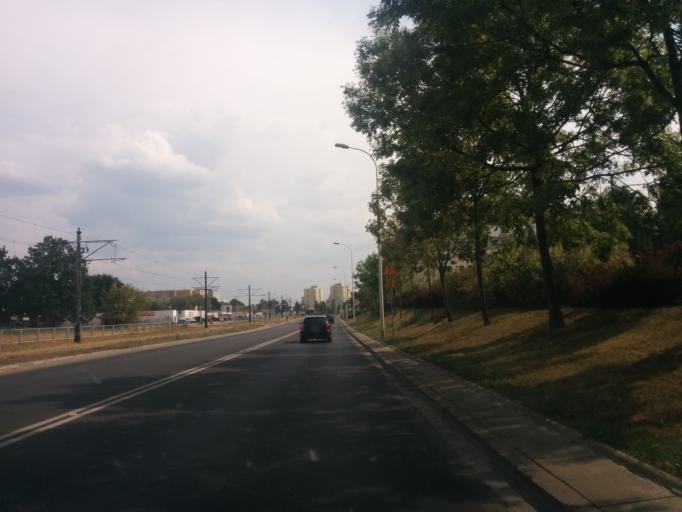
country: PL
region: Masovian Voivodeship
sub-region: Warszawa
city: Bialoleka
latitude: 52.3203
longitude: 20.9487
